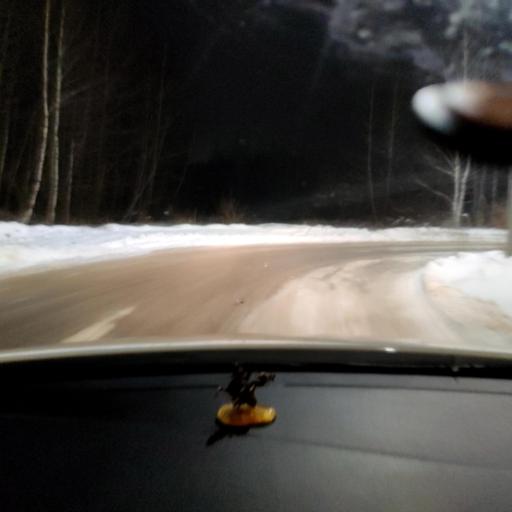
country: RU
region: Tatarstan
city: Stolbishchi
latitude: 55.6785
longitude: 49.1944
